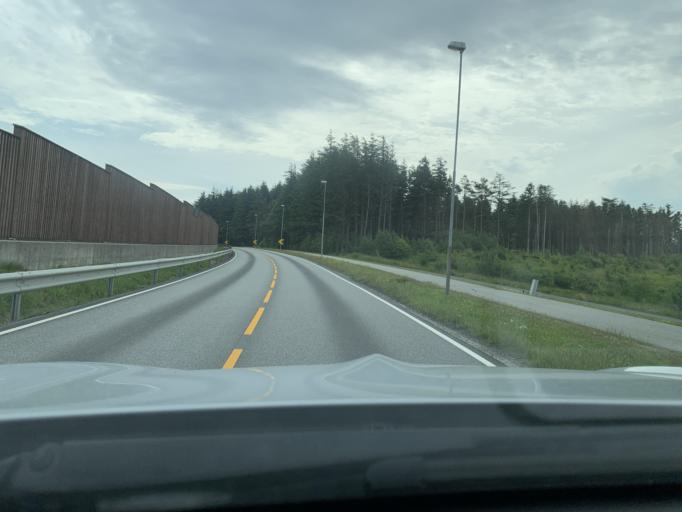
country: NO
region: Rogaland
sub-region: Sandnes
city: Sandnes
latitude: 58.7852
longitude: 5.7069
